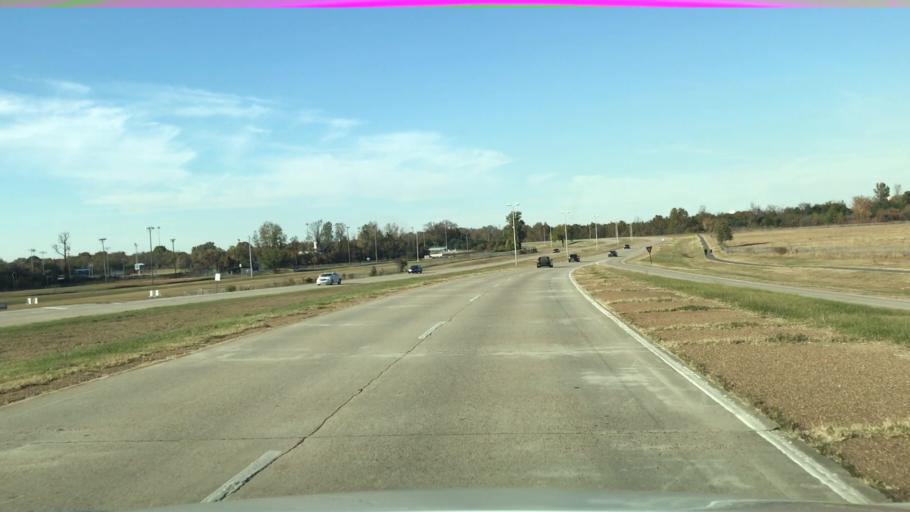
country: US
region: Louisiana
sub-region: Bossier Parish
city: Bossier City
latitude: 32.4783
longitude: -93.6924
